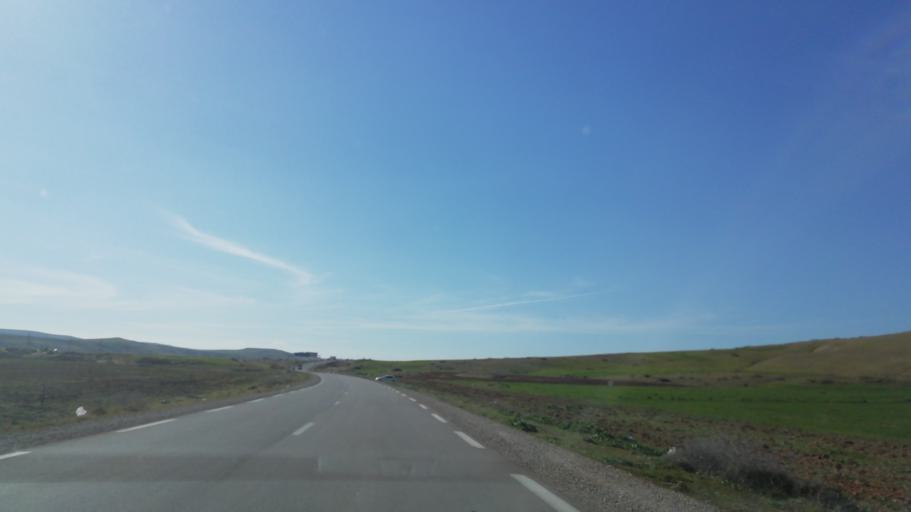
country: DZ
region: Mascara
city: Oued el Abtal
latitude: 35.4448
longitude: 0.8336
